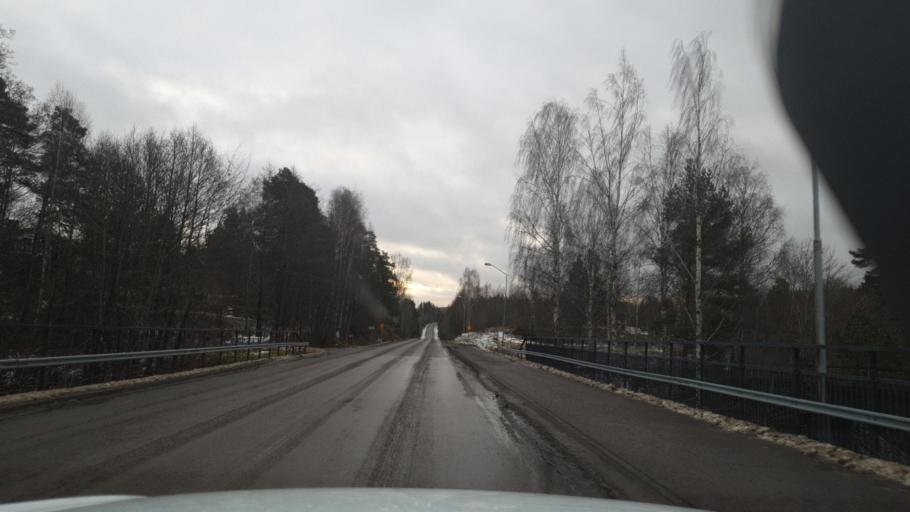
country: SE
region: Vaermland
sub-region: Eda Kommun
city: Amotfors
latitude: 59.7573
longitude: 12.3579
